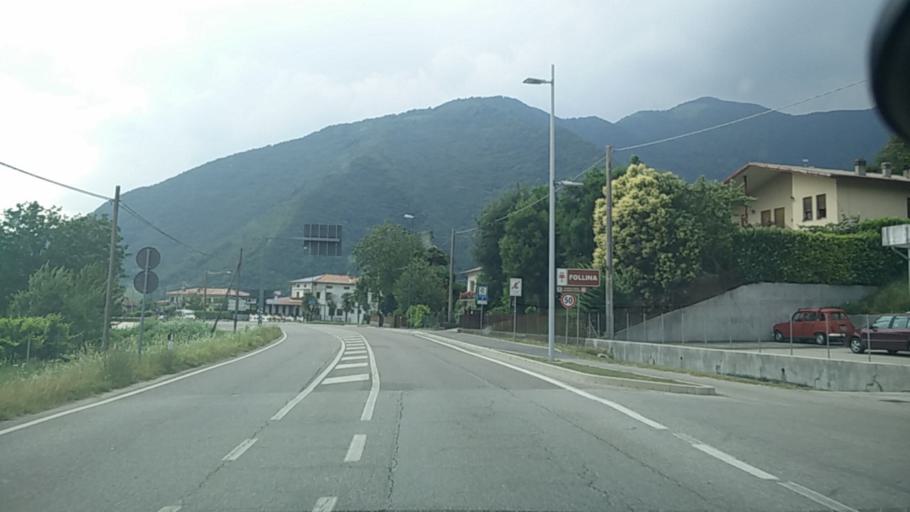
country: IT
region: Veneto
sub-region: Provincia di Treviso
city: Cison di Valmarino
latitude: 45.9659
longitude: 12.1368
